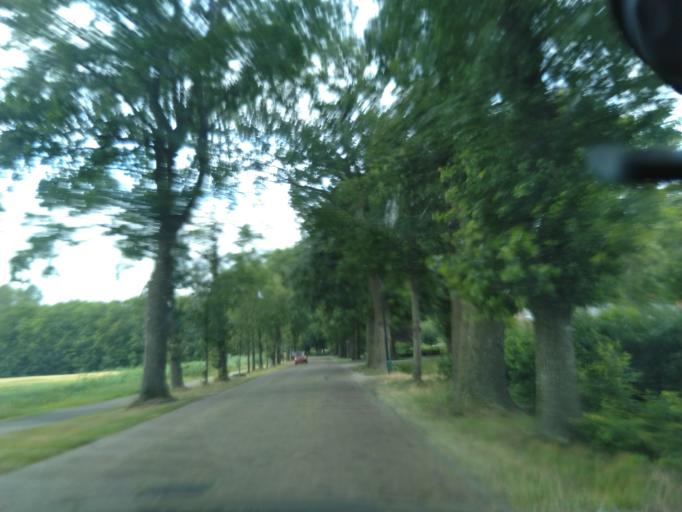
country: NL
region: Groningen
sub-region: Gemeente Vlagtwedde
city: Vlagtwedde
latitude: 53.0924
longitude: 7.1416
